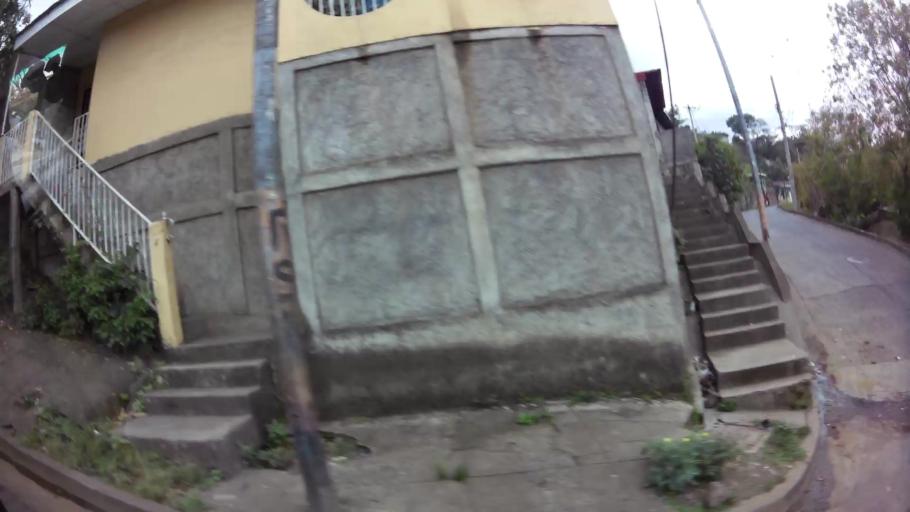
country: NI
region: Matagalpa
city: Matagalpa
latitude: 12.9338
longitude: -85.9150
